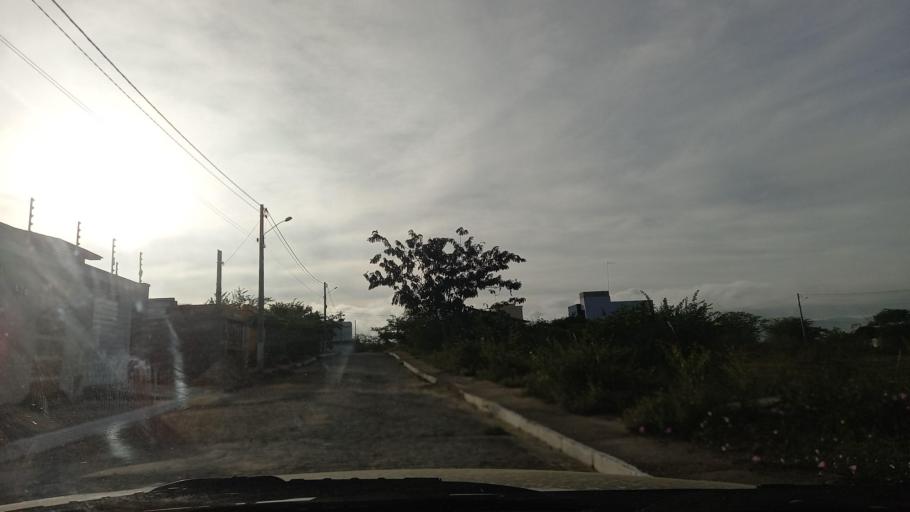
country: BR
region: Pernambuco
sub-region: Bezerros
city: Bezerros
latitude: -8.2174
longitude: -35.7495
